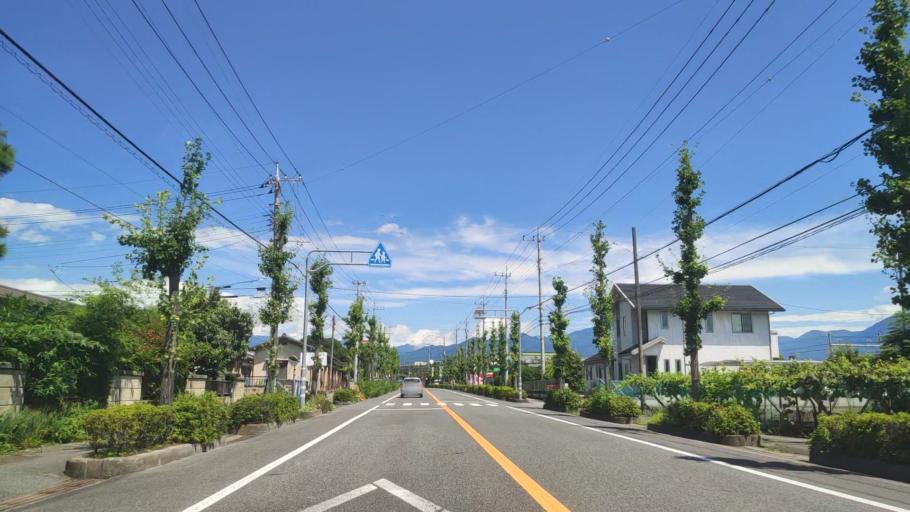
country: JP
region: Yamanashi
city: Isawa
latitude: 35.6581
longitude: 138.6271
